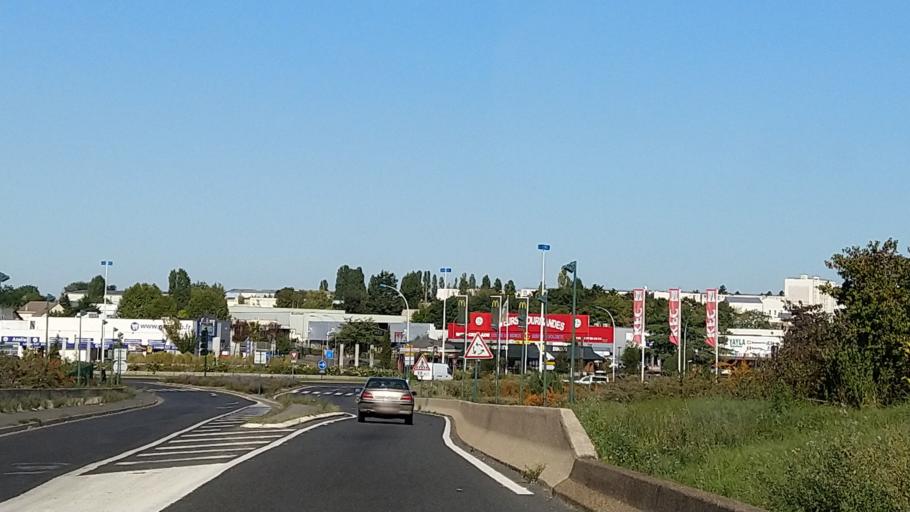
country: FR
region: Ile-de-France
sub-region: Departement du Val-d'Oise
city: Garges-les-Gonesse
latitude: 48.9602
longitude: 2.4041
